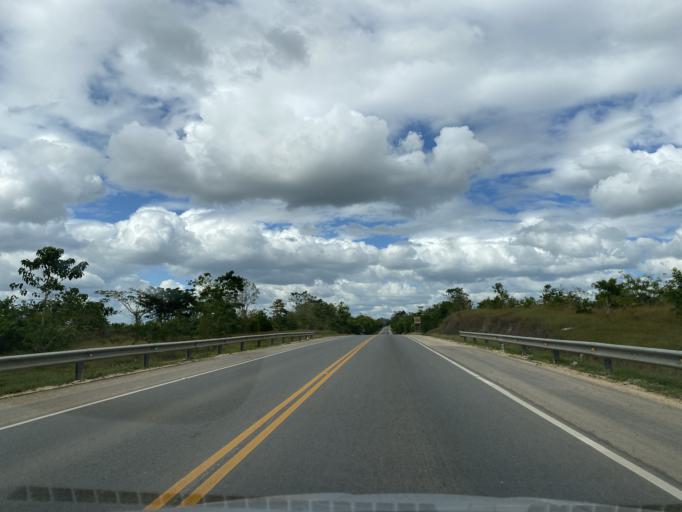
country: DO
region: Santo Domingo
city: Guerra
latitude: 18.5442
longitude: -69.7599
